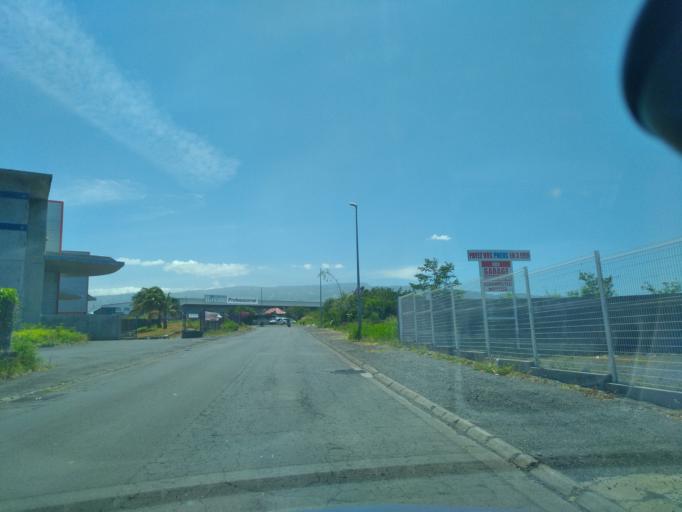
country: RE
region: Reunion
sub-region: Reunion
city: Saint-Pierre
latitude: -21.3204
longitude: 55.4502
